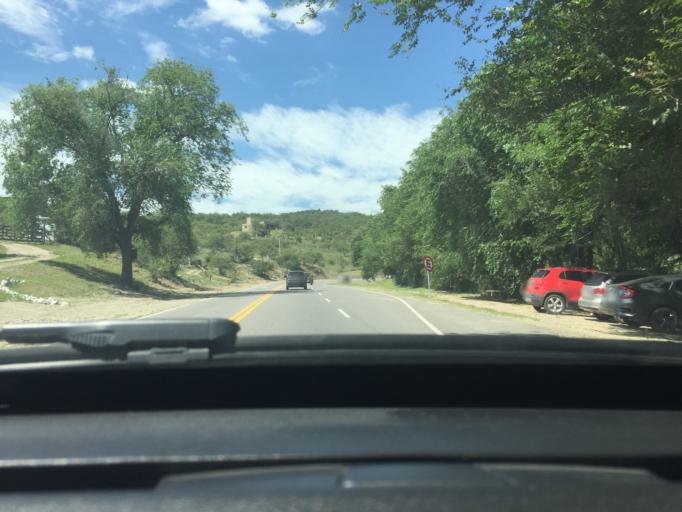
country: AR
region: Cordoba
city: Alta Gracia
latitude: -31.7386
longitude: -64.4530
